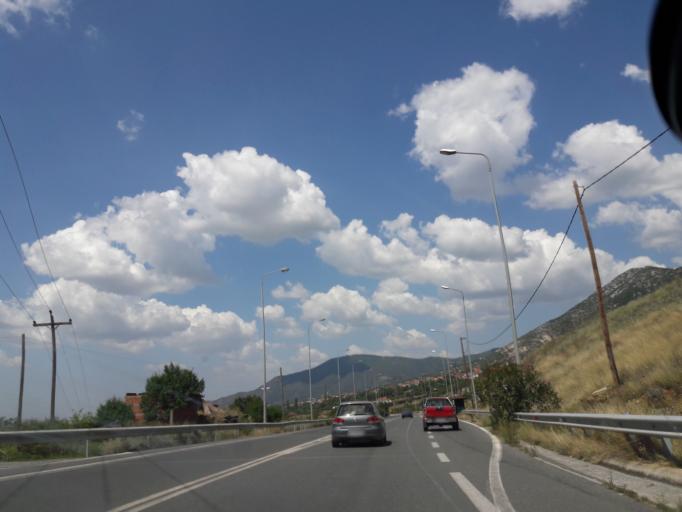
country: GR
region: Central Macedonia
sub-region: Nomos Chalkidikis
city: Galatista
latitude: 40.4579
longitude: 23.2901
